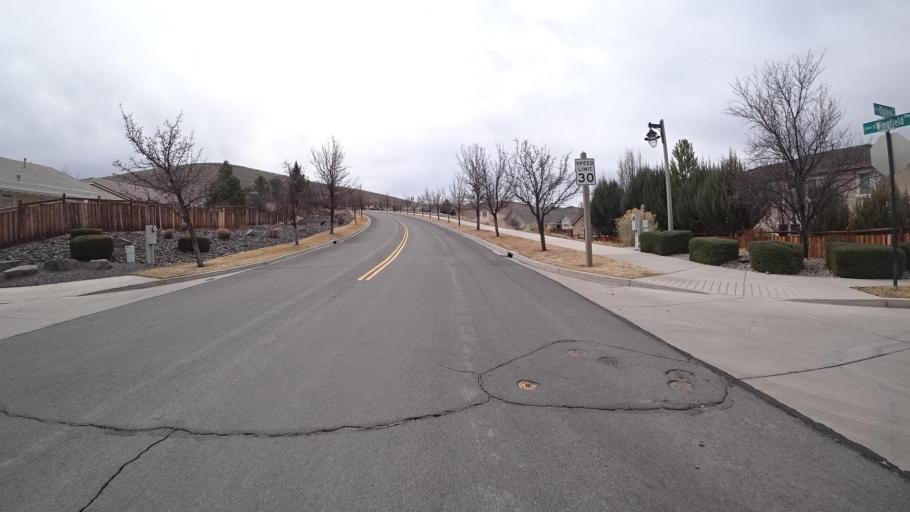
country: US
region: Nevada
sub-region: Washoe County
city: Spanish Springs
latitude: 39.6051
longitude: -119.6866
